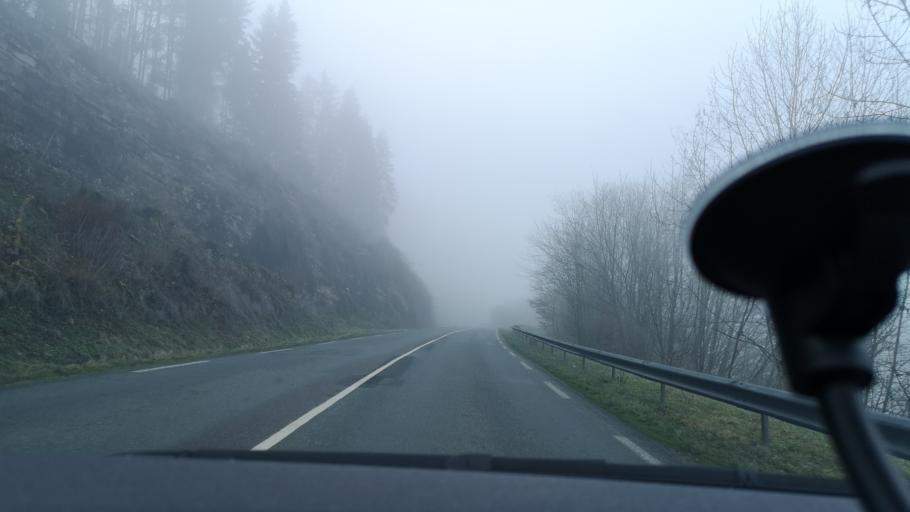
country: FR
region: Franche-Comte
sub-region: Departement du Doubs
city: Clerval
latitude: 47.4128
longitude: 6.5522
